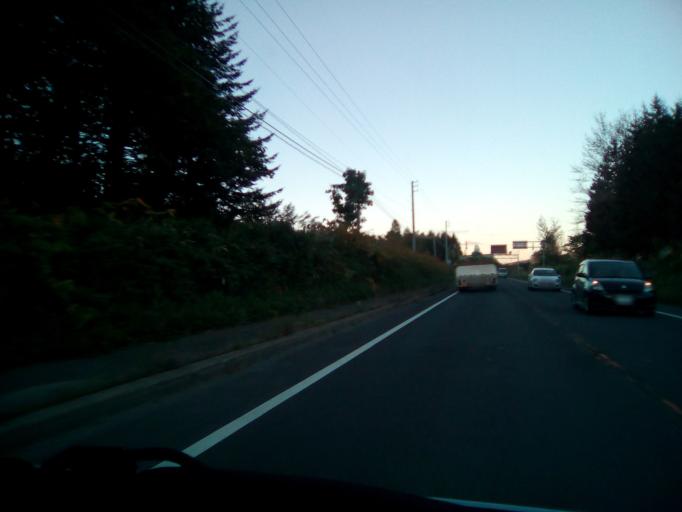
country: JP
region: Hokkaido
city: Niseko Town
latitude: 42.6955
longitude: 140.8406
